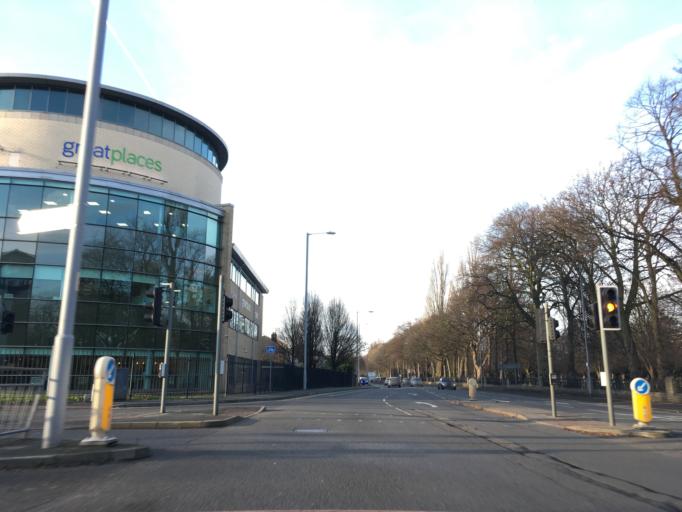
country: GB
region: England
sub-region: Manchester
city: Chorlton cum Hardy
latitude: 53.4262
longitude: -2.2583
